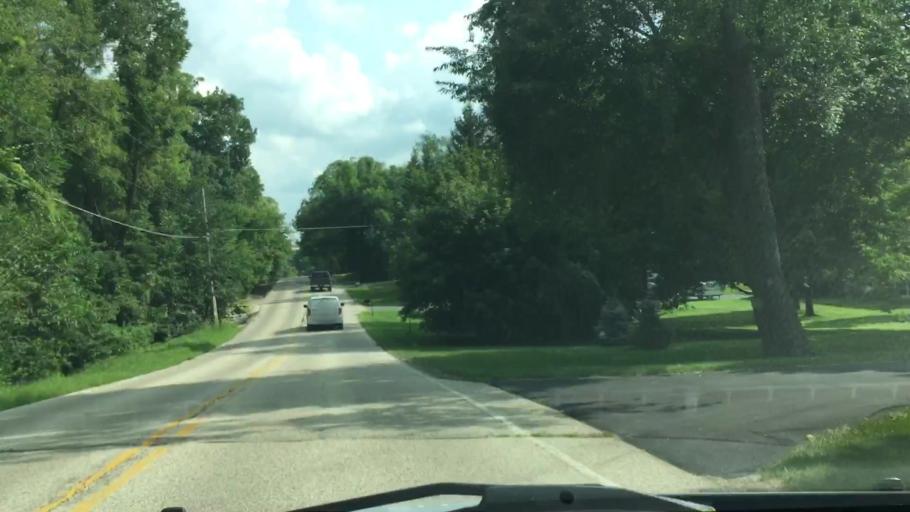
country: US
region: Wisconsin
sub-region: Waukesha County
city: Wales
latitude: 43.0441
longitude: -88.3496
